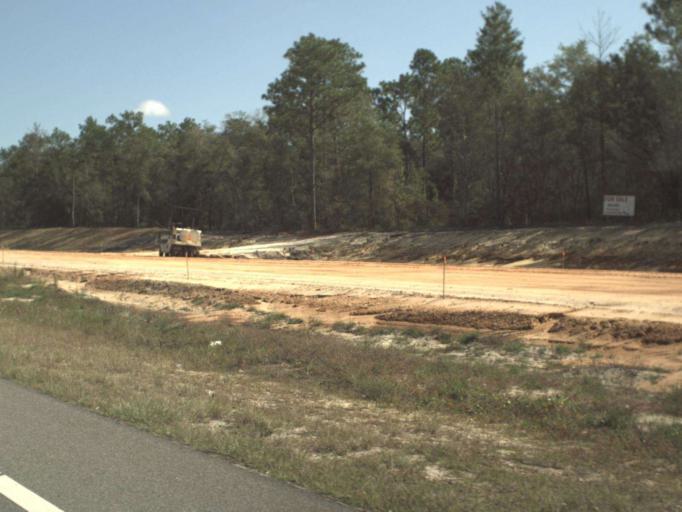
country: US
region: Florida
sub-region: Walton County
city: Freeport
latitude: 30.5025
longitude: -86.1167
